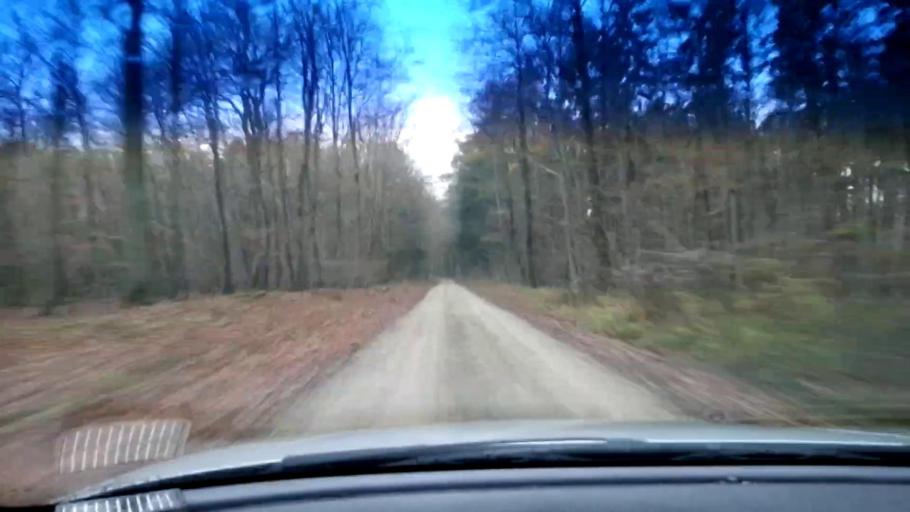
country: DE
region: Bavaria
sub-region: Upper Franconia
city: Schesslitz
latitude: 49.9455
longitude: 11.0224
